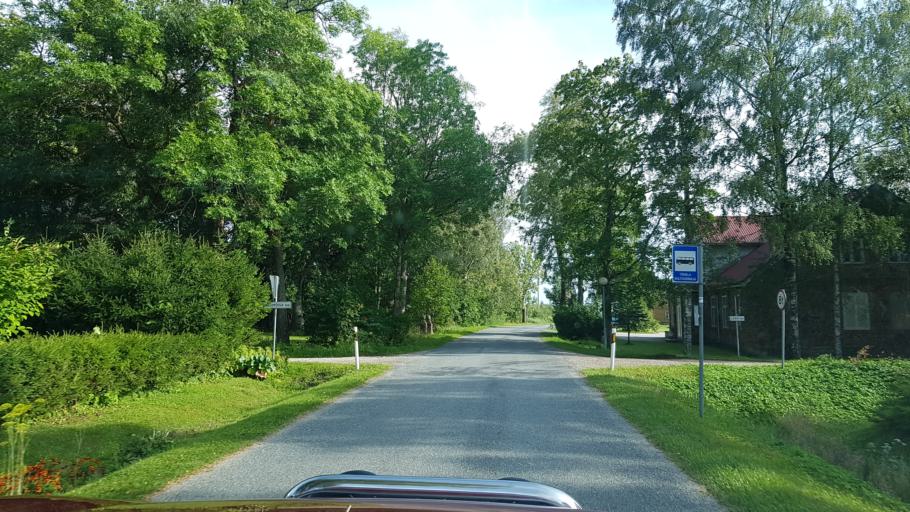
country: EE
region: Laeaene
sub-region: Lihula vald
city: Lihula
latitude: 58.4397
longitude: 24.0047
